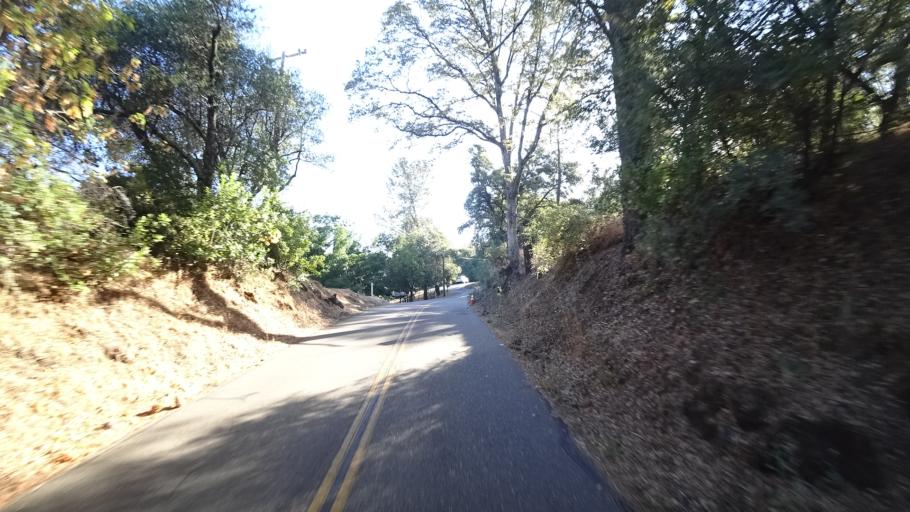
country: US
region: California
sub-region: Amador County
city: Jackson
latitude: 38.3009
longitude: -120.7152
